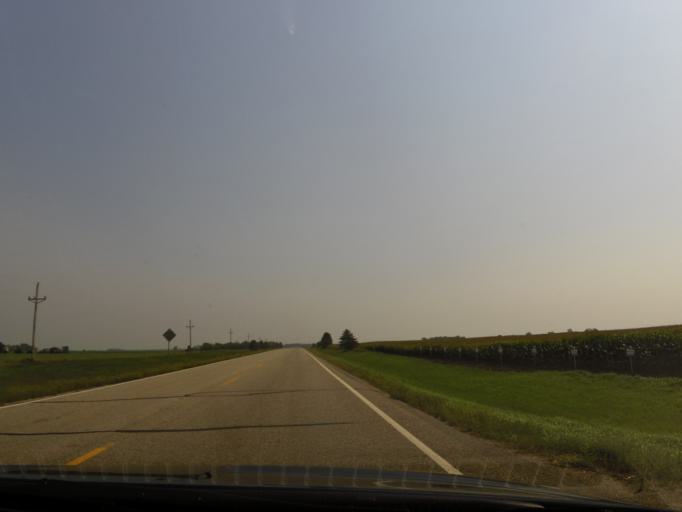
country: US
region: South Dakota
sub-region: Roberts County
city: Sisseton
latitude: 46.0688
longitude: -97.1472
